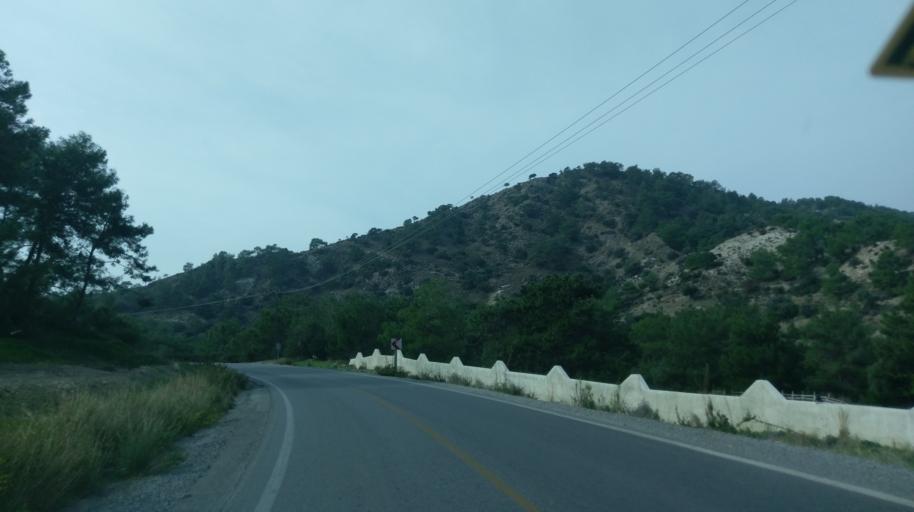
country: CY
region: Keryneia
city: Lapithos
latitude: 35.3429
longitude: 33.0760
